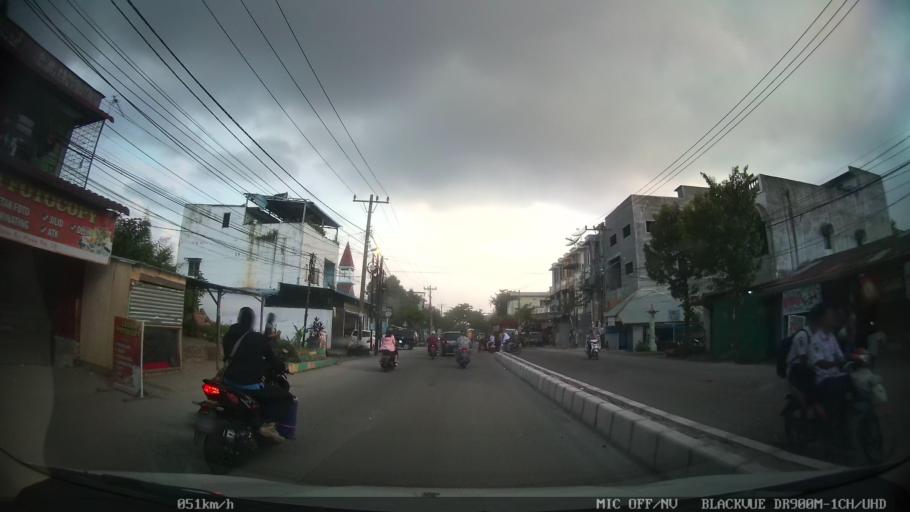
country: ID
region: North Sumatra
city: Medan
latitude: 3.5864
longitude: 98.7113
